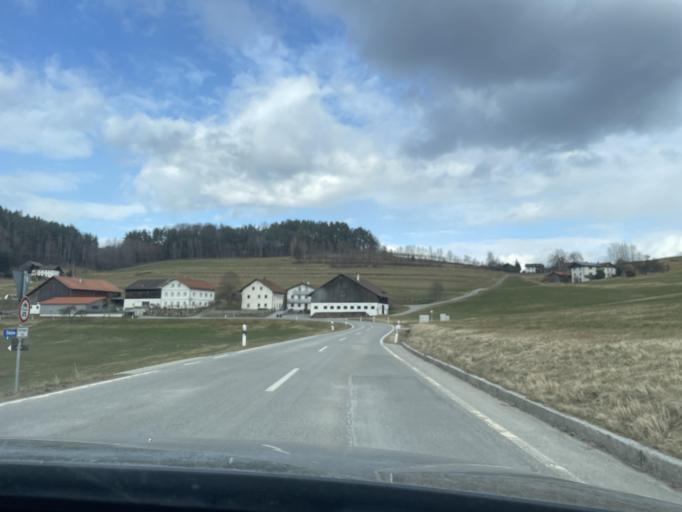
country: DE
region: Bavaria
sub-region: Lower Bavaria
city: Viechtach
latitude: 49.0884
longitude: 12.9023
